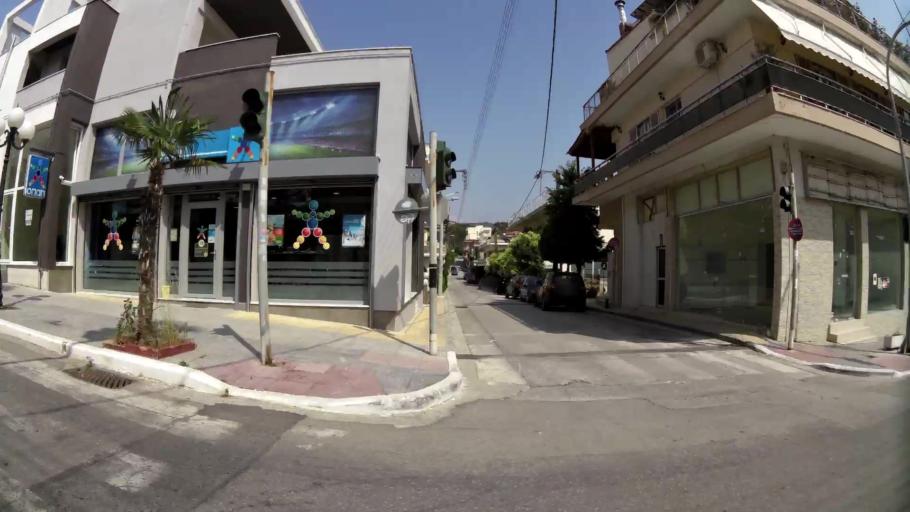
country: GR
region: Central Macedonia
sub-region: Nomos Thessalonikis
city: Efkarpia
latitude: 40.6878
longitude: 22.9543
